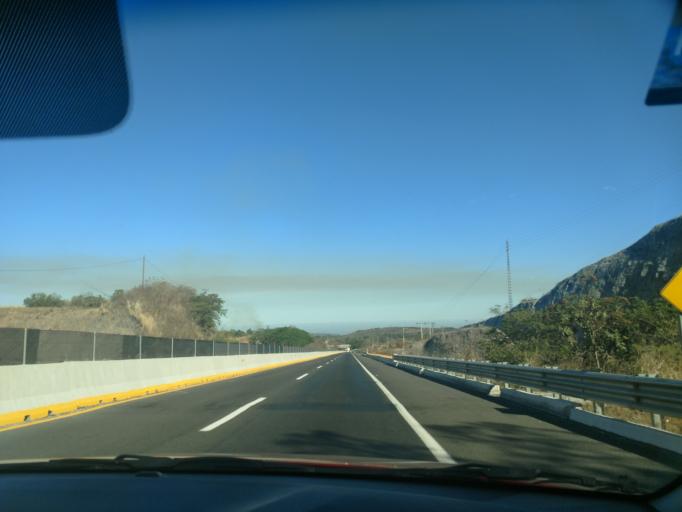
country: MX
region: Nayarit
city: Tepic
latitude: 21.5618
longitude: -104.9721
